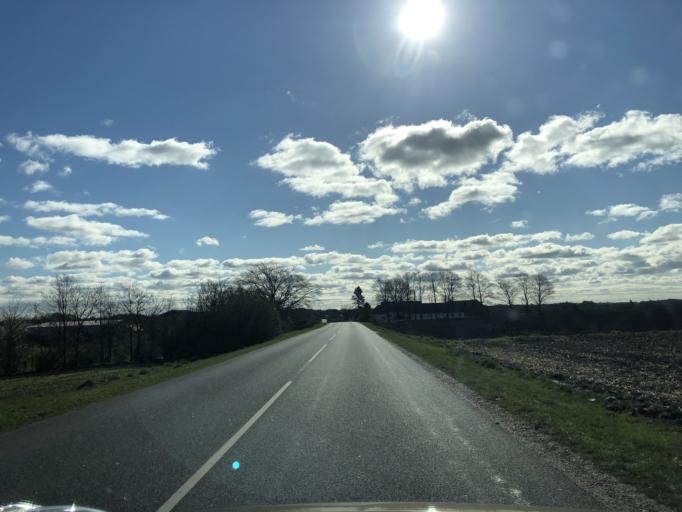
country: DK
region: North Denmark
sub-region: Vesthimmerland Kommune
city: Alestrup
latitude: 56.6159
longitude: 9.5144
